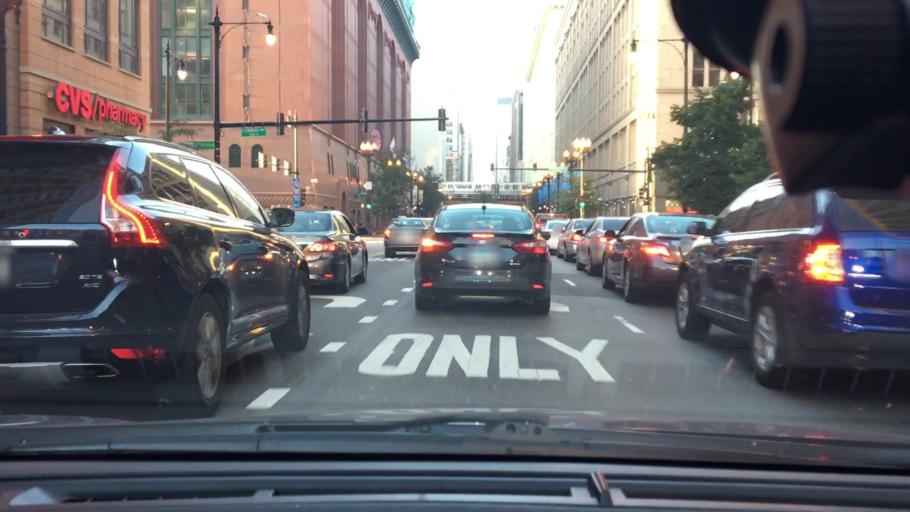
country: US
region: Illinois
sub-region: Cook County
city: Chicago
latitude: 41.8751
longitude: -87.6276
